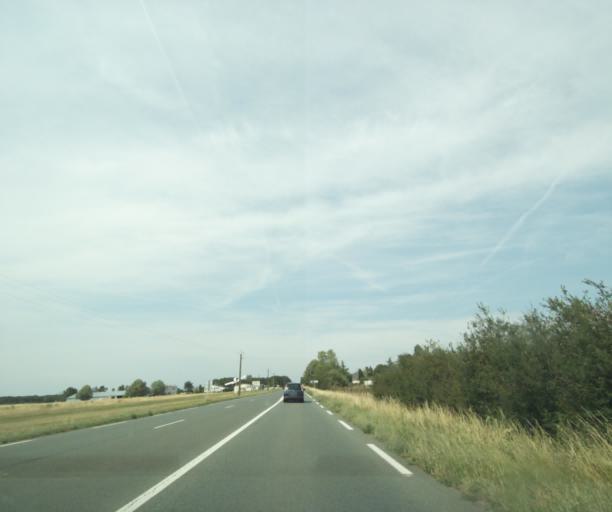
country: FR
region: Centre
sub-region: Departement d'Indre-et-Loire
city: Montbazon
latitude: 47.2657
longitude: 0.7049
